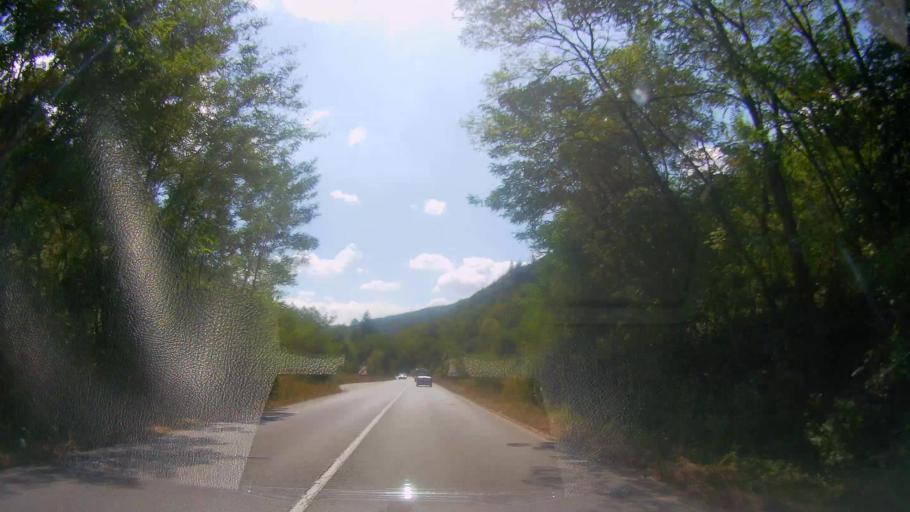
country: BG
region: Stara Zagora
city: Gurkovo
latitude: 42.7480
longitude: 25.7096
